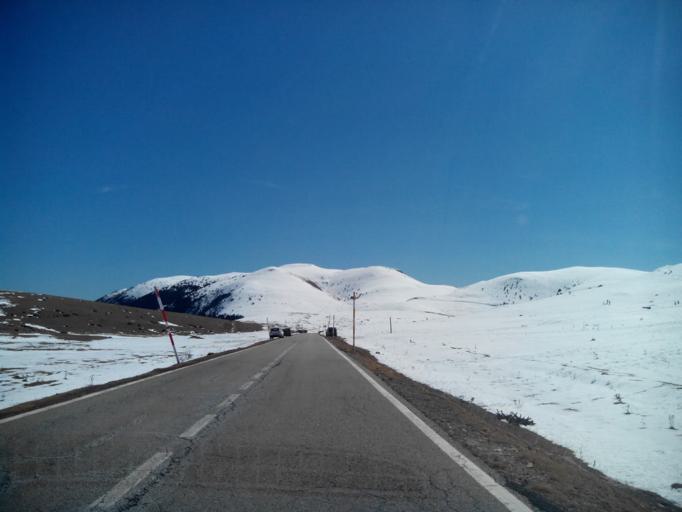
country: ES
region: Catalonia
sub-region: Provincia de Girona
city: Toses
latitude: 42.3216
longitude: 1.9635
